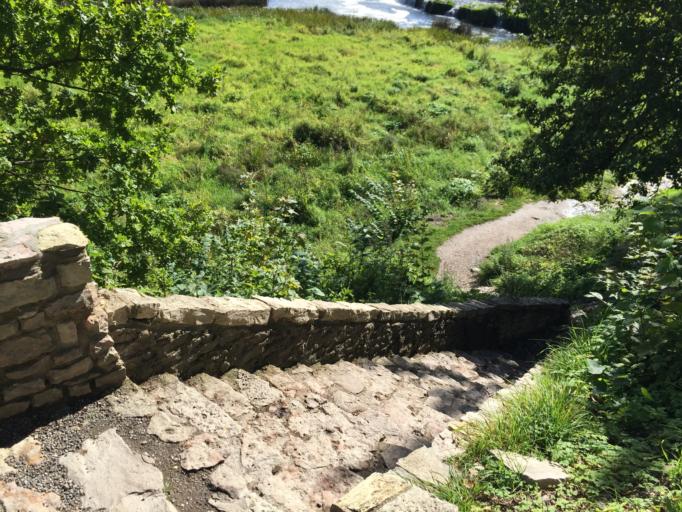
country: LV
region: Kuldigas Rajons
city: Kuldiga
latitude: 56.9684
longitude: 21.9770
